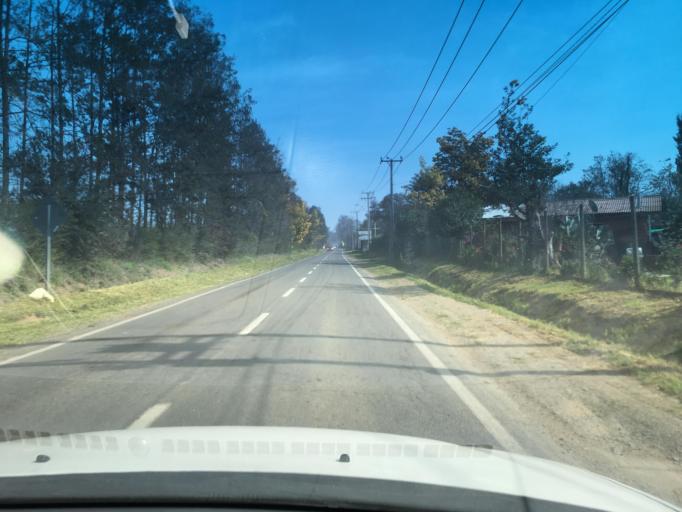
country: CL
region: Valparaiso
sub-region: Provincia de Marga Marga
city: Limache
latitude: -33.0173
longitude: -71.1797
